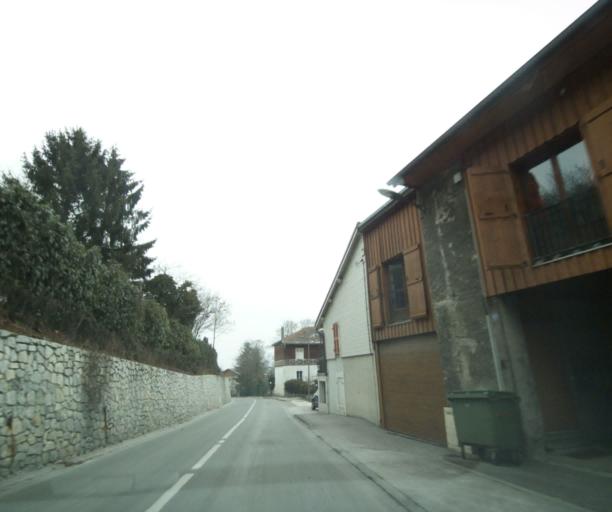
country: FR
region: Rhone-Alpes
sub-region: Departement de la Haute-Savoie
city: Vetraz-Monthoux
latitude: 46.1655
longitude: 6.2378
